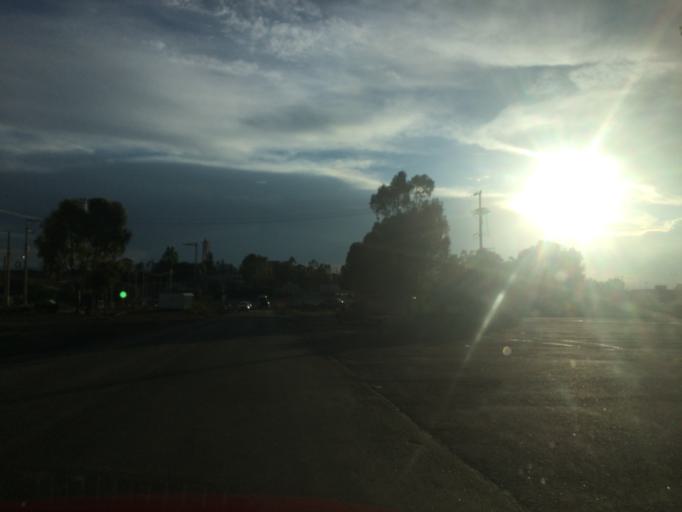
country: MX
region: Zacatecas
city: Zacatecas
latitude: 22.7699
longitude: -102.6120
